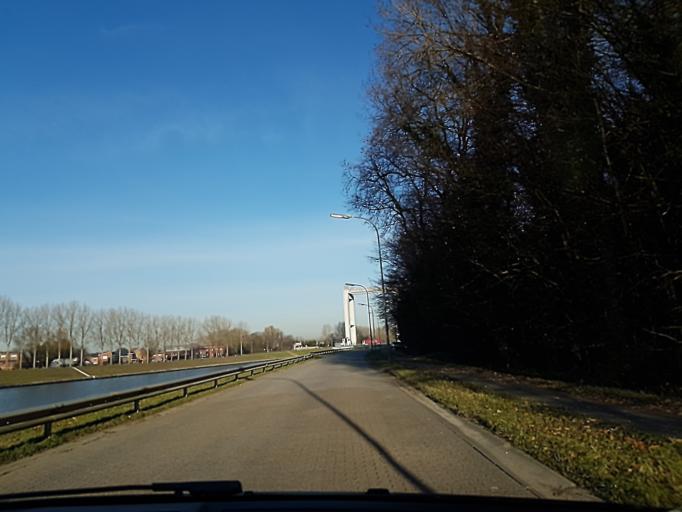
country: BE
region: Flanders
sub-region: Provincie Vlaams-Brabant
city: Kapelle-op-den-Bos
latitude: 51.0302
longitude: 4.3582
